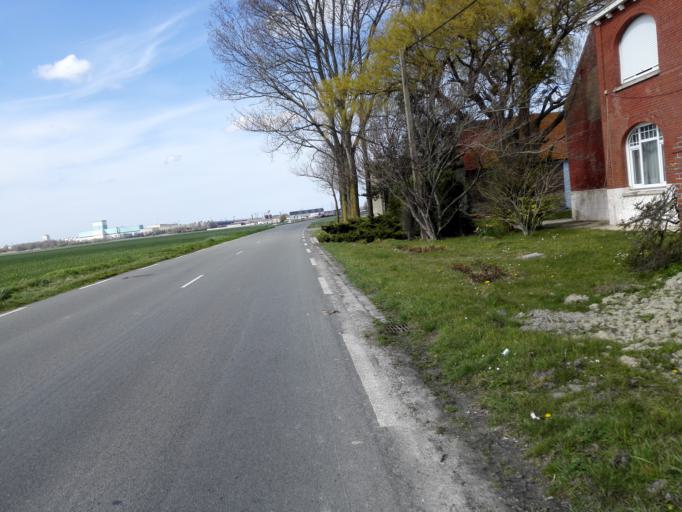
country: FR
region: Nord-Pas-de-Calais
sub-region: Departement du Nord
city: Spycker
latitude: 50.9765
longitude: 2.3096
